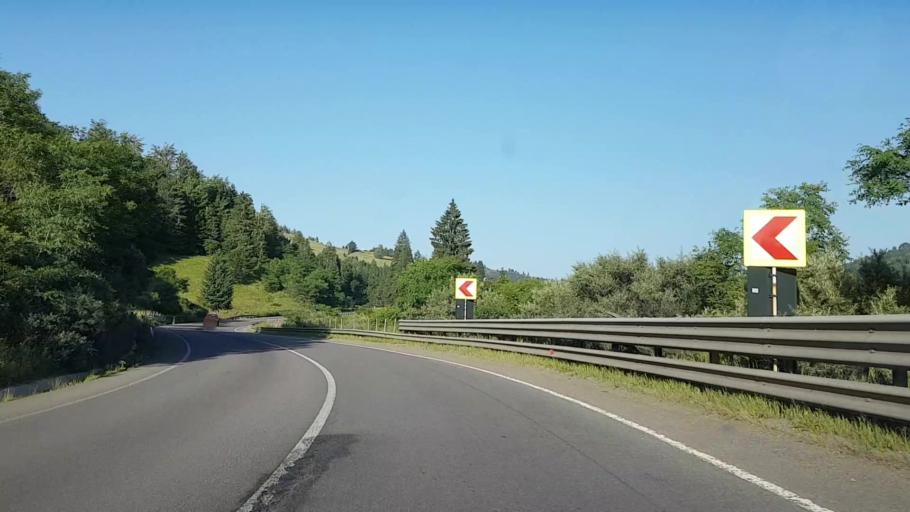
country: RO
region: Bistrita-Nasaud
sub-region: Comuna Tiha Bargaului
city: Tureac
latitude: 47.2216
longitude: 24.9350
